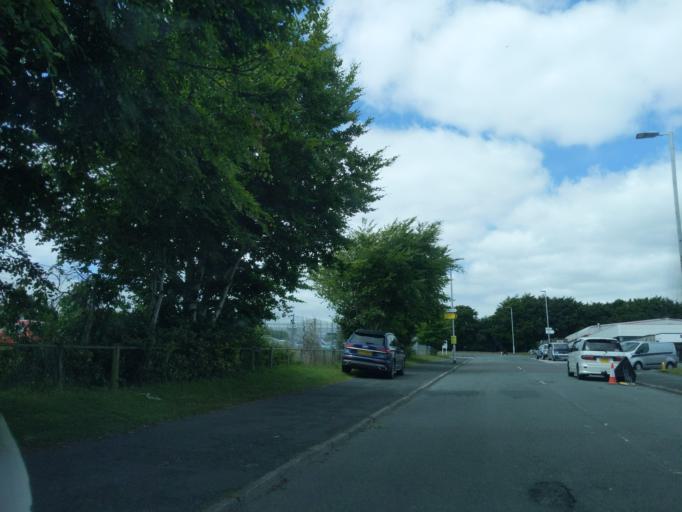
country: GB
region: England
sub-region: Devon
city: Plympton
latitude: 50.4200
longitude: -4.0904
